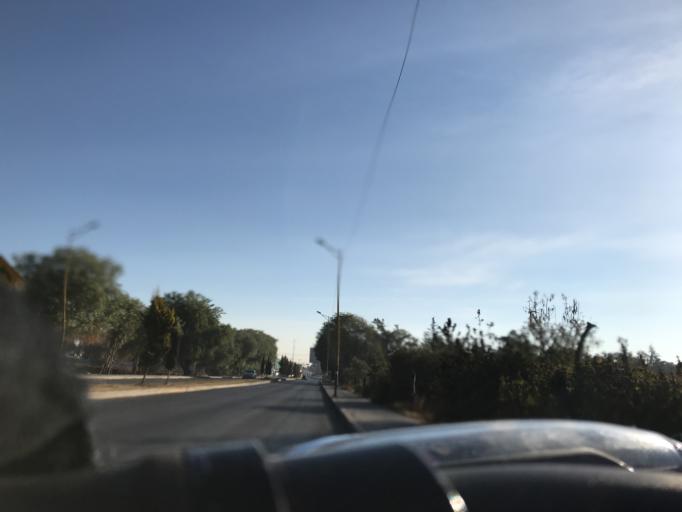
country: MX
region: Mexico
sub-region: Tultepec
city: Tultepec
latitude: 19.6787
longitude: -99.1466
